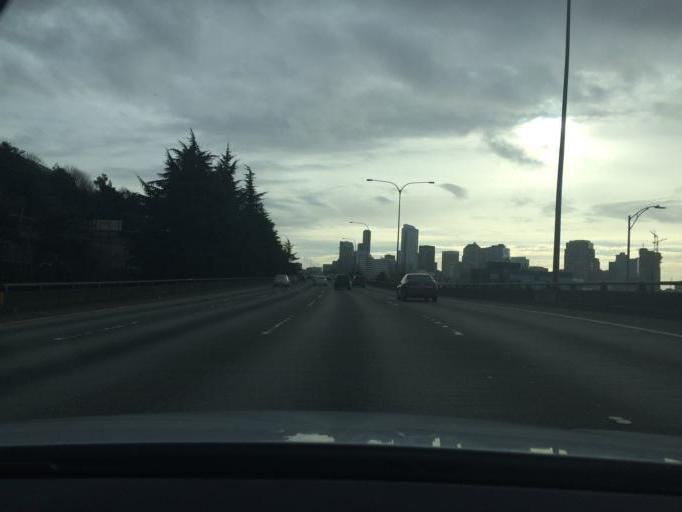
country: US
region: Washington
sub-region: King County
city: Seattle
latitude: 47.6274
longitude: -122.3286
